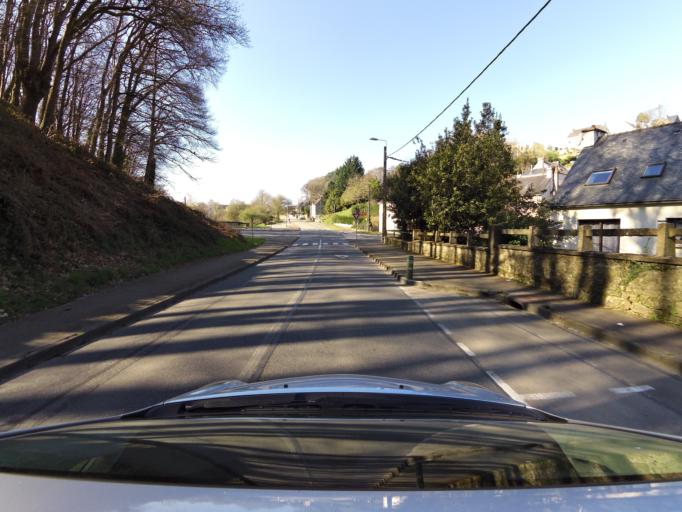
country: FR
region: Brittany
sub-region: Departement du Morbihan
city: Hennebont
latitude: 47.8166
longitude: -3.2569
